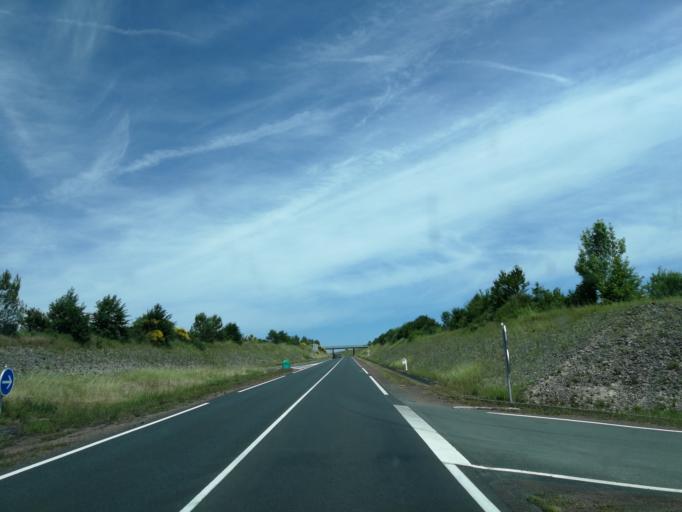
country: FR
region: Pays de la Loire
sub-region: Departement de la Vendee
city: Serigne
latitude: 46.4944
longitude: -0.8301
